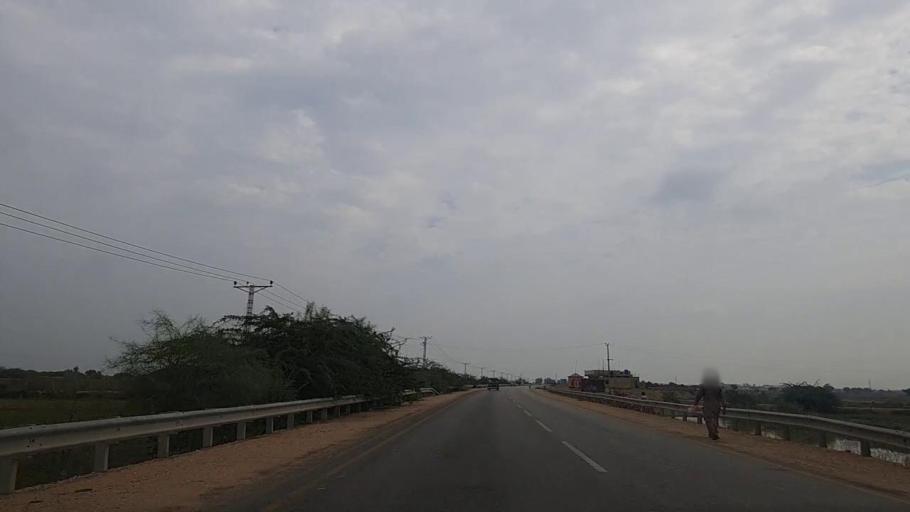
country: PK
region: Sindh
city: Thatta
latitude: 24.6185
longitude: 68.0766
